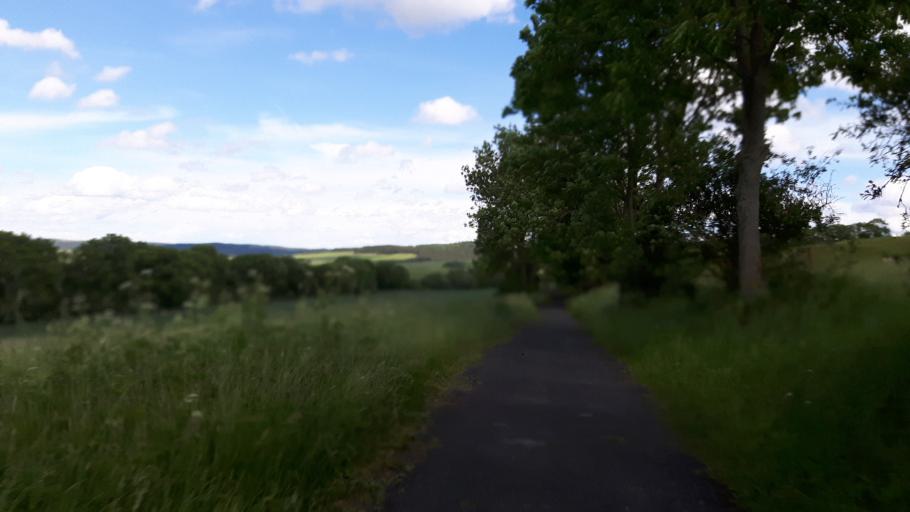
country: DE
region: Thuringia
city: Witzleben
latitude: 50.7830
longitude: 11.1190
